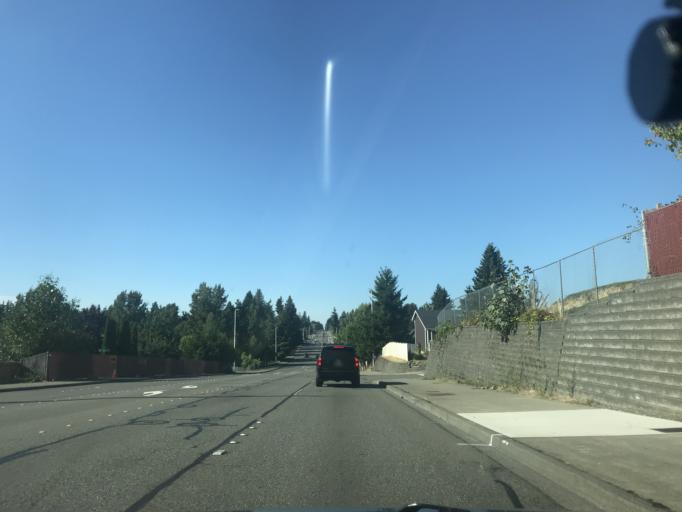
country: US
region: Washington
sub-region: King County
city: Lea Hill
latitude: 47.3632
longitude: -122.1867
